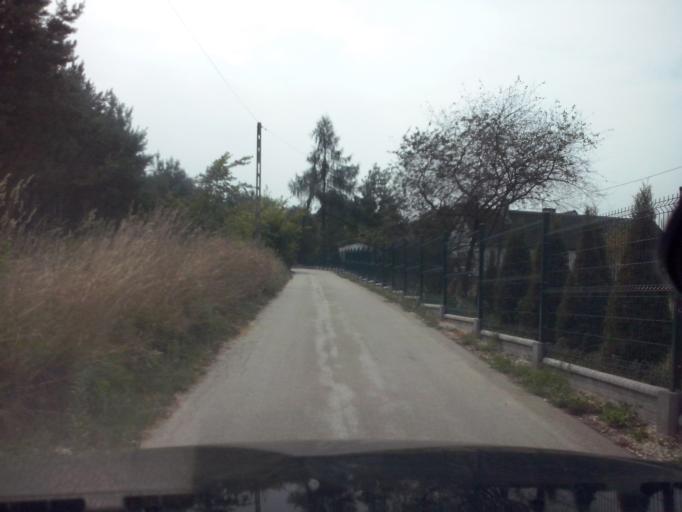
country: PL
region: Swietokrzyskie
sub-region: Powiat kielecki
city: Brzeziny
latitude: 50.7509
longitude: 20.5451
